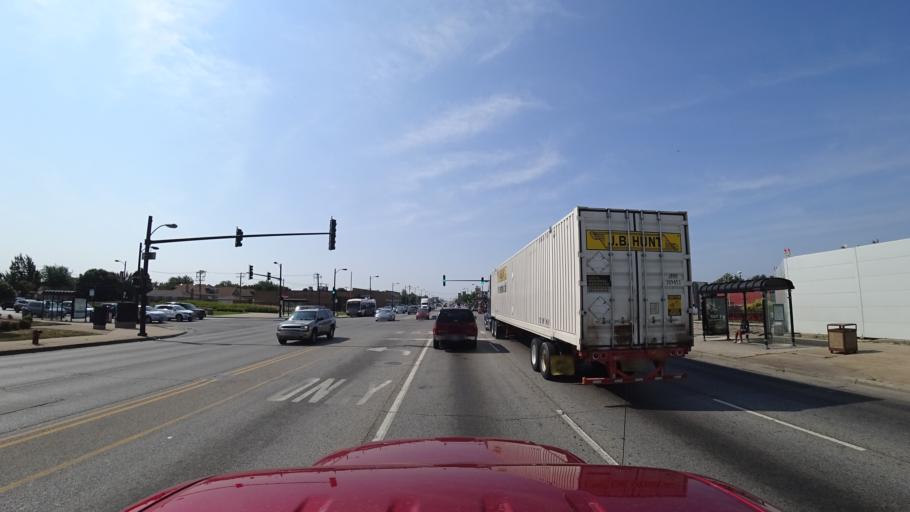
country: US
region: Illinois
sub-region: Cook County
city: Hometown
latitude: 41.7789
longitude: -87.7424
